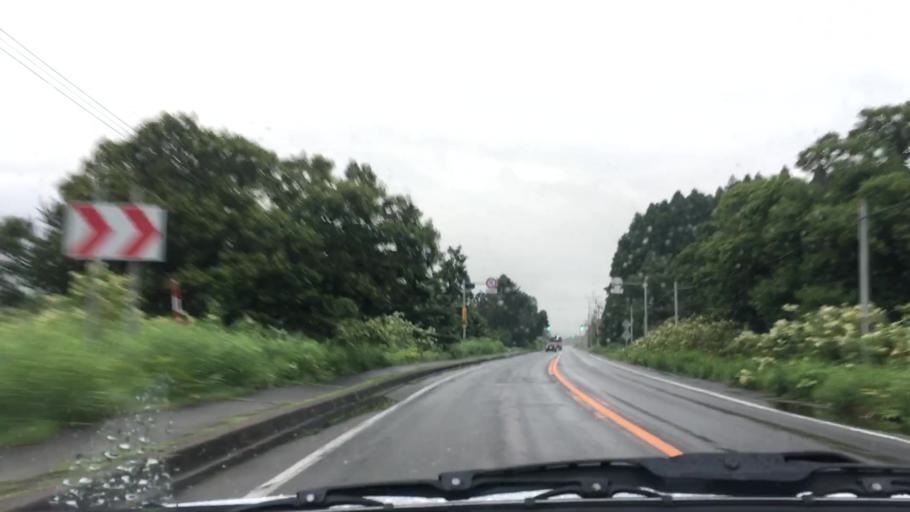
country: JP
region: Hokkaido
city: Nanae
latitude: 42.1767
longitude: 140.4510
